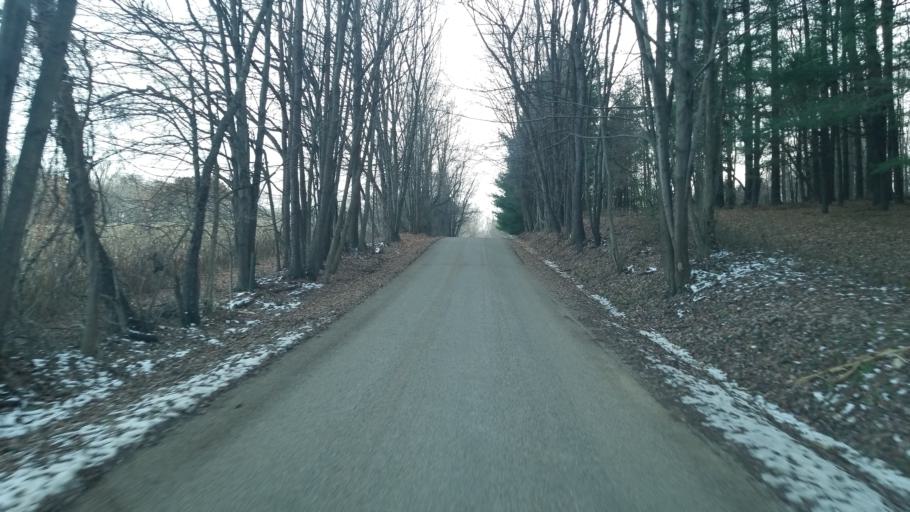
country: US
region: Ohio
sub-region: Sandusky County
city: Bellville
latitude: 40.6558
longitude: -82.4270
